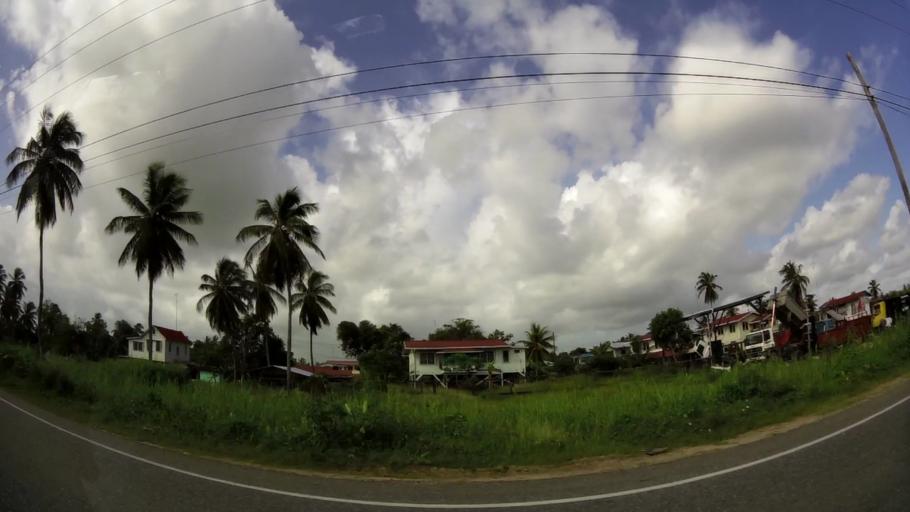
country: GY
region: Demerara-Mahaica
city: Mahaica Village
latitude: 6.6785
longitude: -57.9238
